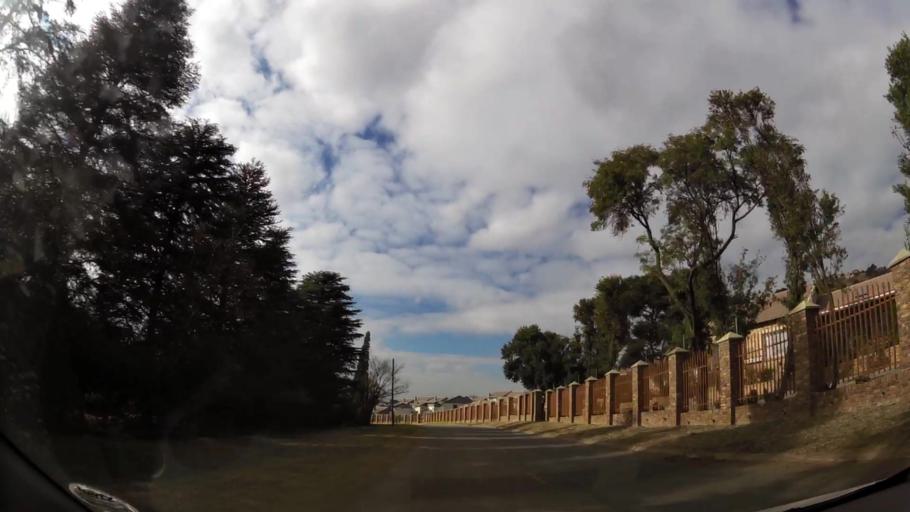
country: ZA
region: Gauteng
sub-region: City of Johannesburg Metropolitan Municipality
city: Roodepoort
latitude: -26.1028
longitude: 27.8696
